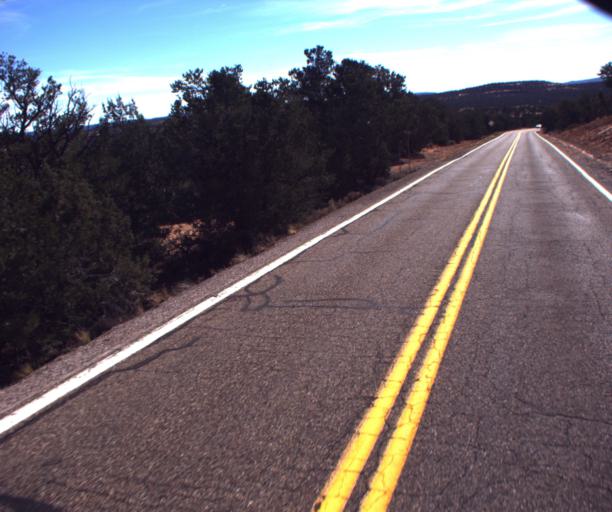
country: US
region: Arizona
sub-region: Navajo County
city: Kayenta
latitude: 36.6658
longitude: -110.5286
